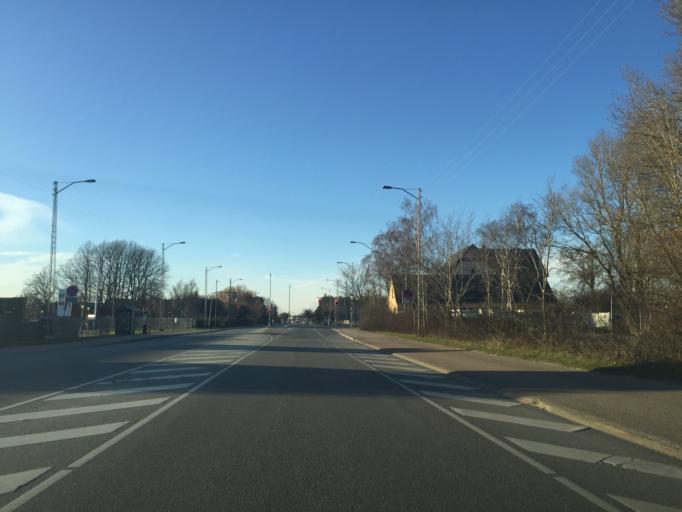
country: DK
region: Capital Region
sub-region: Tarnby Kommune
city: Tarnby
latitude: 55.6083
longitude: 12.6157
